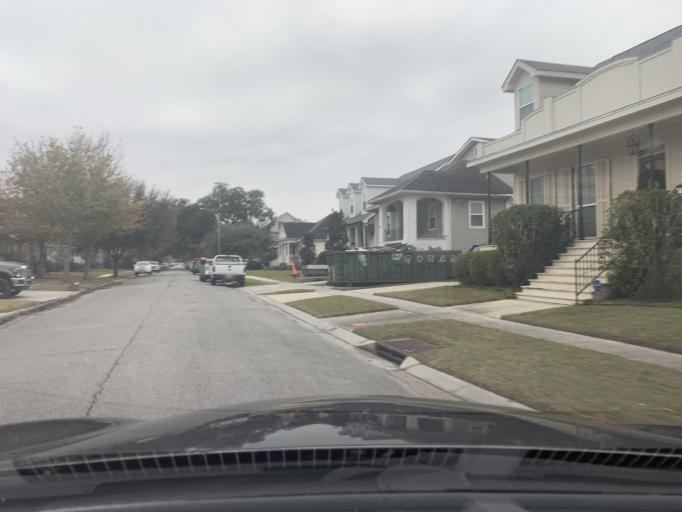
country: US
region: Louisiana
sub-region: Jefferson Parish
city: Metairie
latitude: 30.0125
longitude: -90.1105
